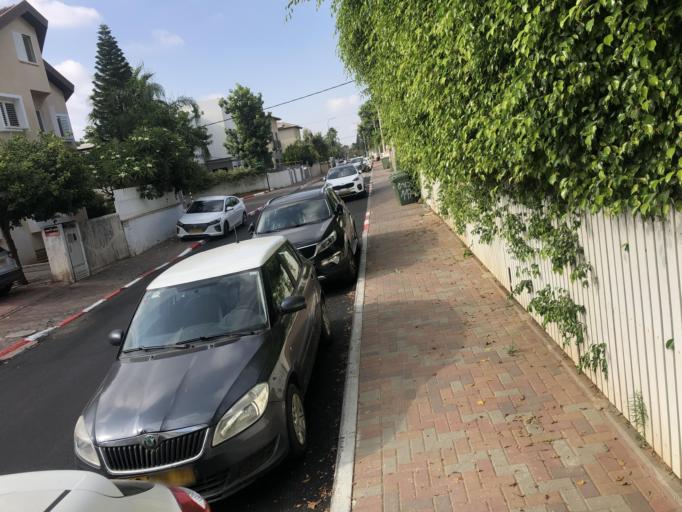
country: IL
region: Central District
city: Yehud
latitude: 32.0390
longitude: 34.8843
